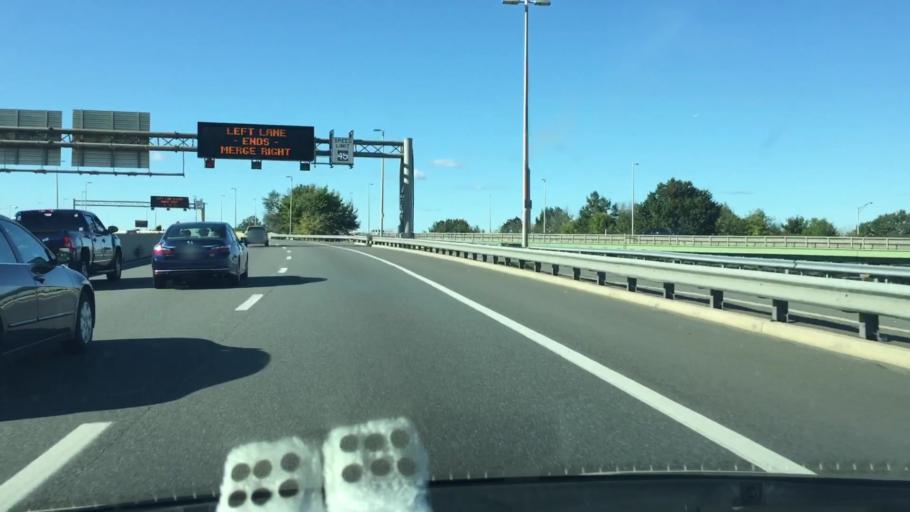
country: US
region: New Jersey
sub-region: Camden County
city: Gloucester City
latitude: 39.9010
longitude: -75.1115
